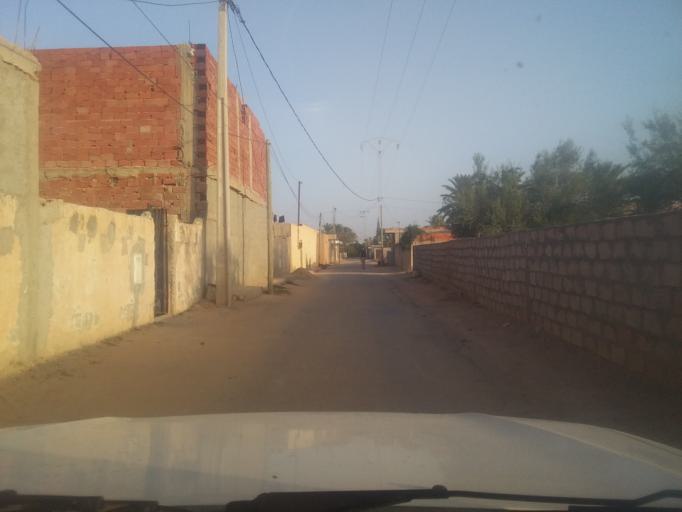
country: TN
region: Qabis
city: Gabes
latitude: 33.6222
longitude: 10.2954
